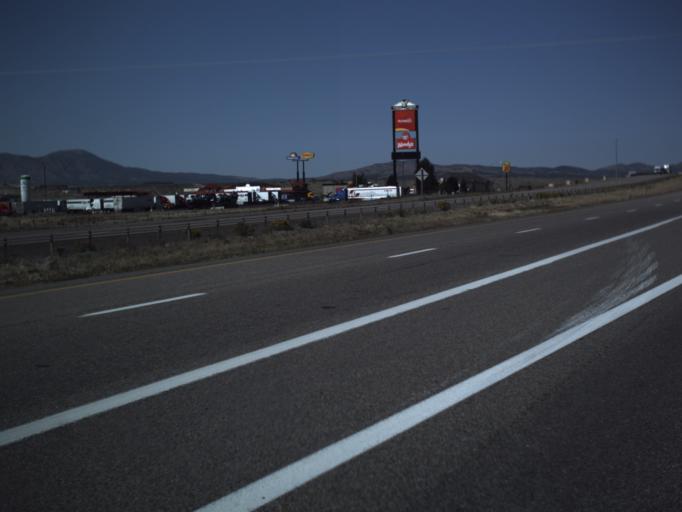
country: US
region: Utah
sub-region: Beaver County
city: Beaver
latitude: 38.2887
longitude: -112.6504
